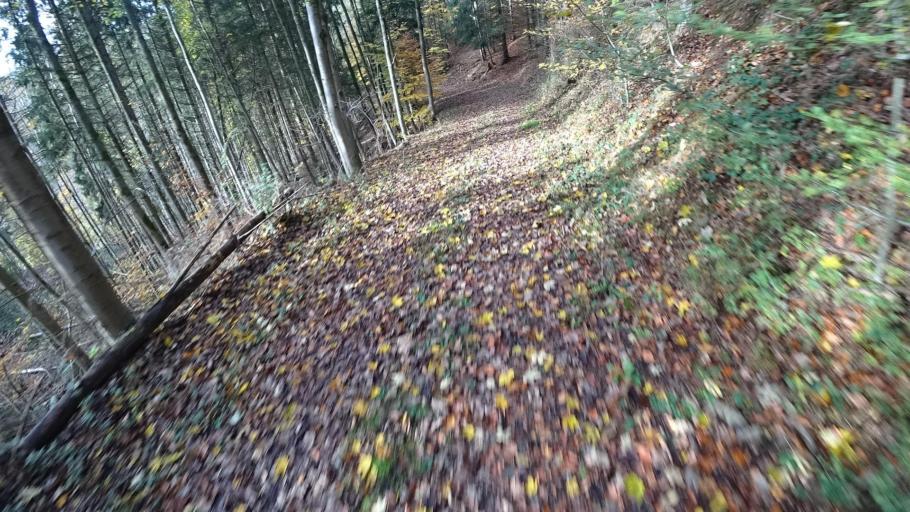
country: DE
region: Rheinland-Pfalz
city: Lind
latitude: 50.4895
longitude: 6.9201
